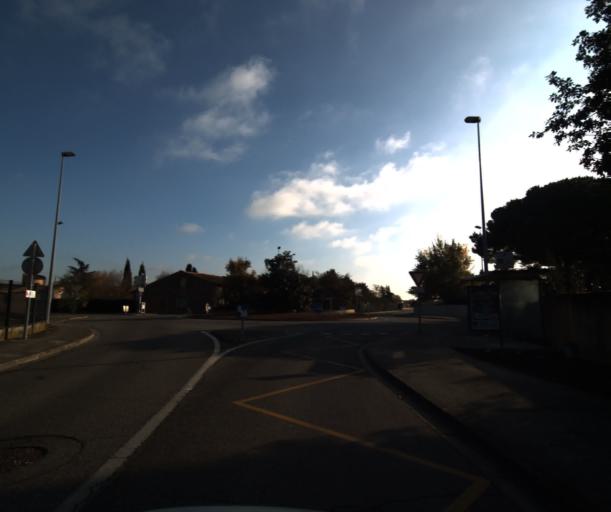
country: FR
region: Midi-Pyrenees
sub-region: Departement de la Haute-Garonne
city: Colomiers
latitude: 43.5928
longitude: 1.3587
